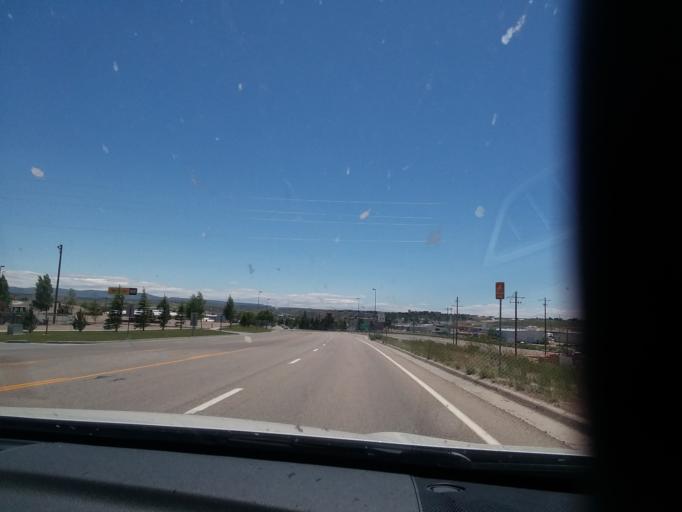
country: US
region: Wyoming
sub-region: Sweetwater County
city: North Rock Springs
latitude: 41.6233
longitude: -109.2333
